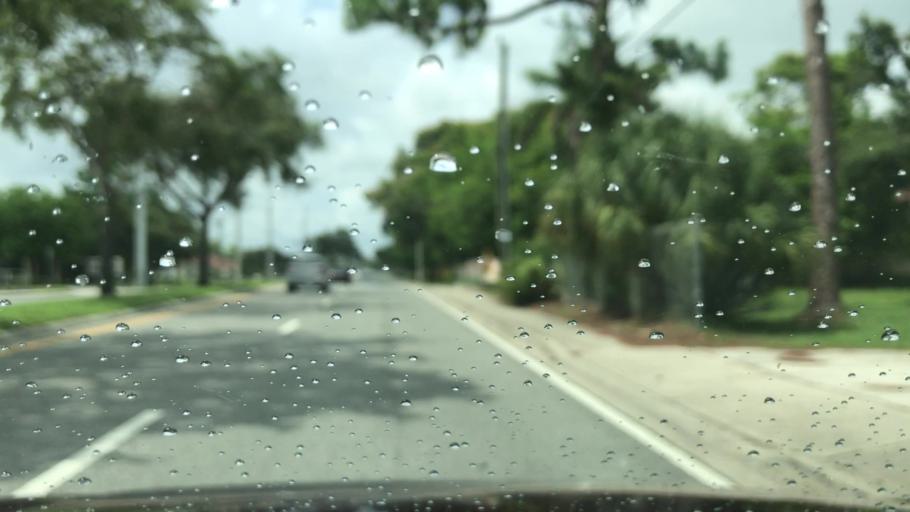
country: US
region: Florida
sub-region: Sarasota County
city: Vamo
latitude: 27.2398
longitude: -82.4975
